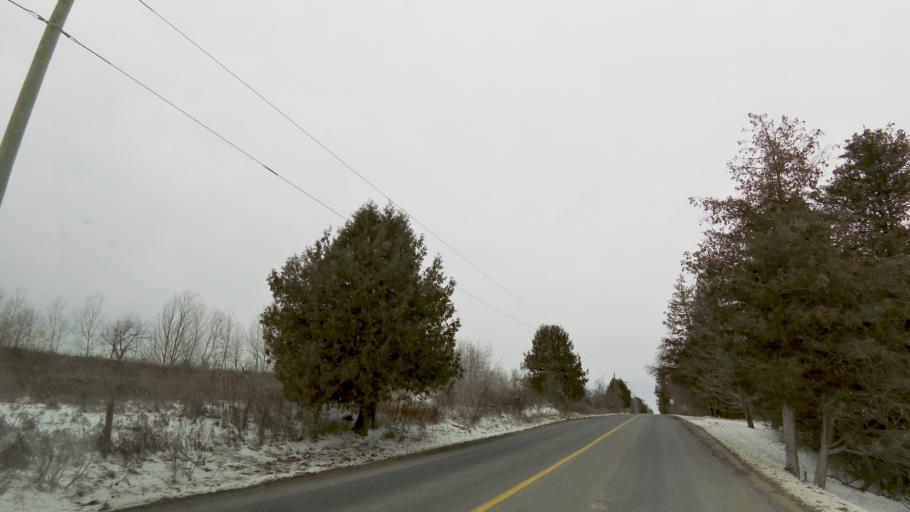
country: CA
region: Ontario
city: Bradford West Gwillimbury
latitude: 43.9622
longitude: -79.6414
